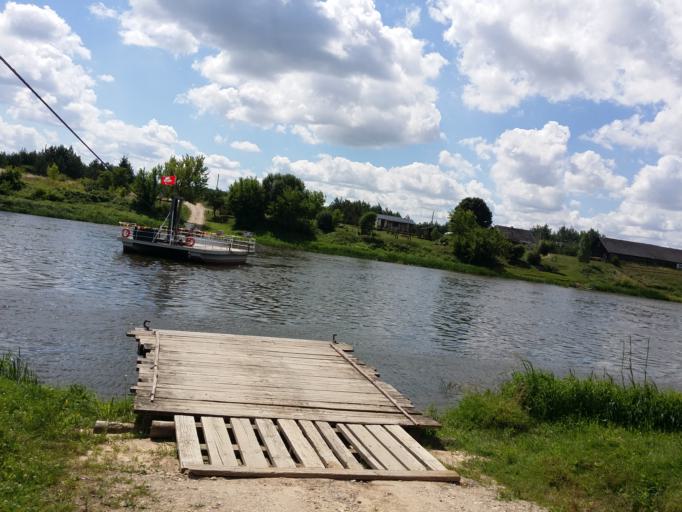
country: LT
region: Vilnius County
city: Elektrenai
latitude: 54.9485
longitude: 24.6753
